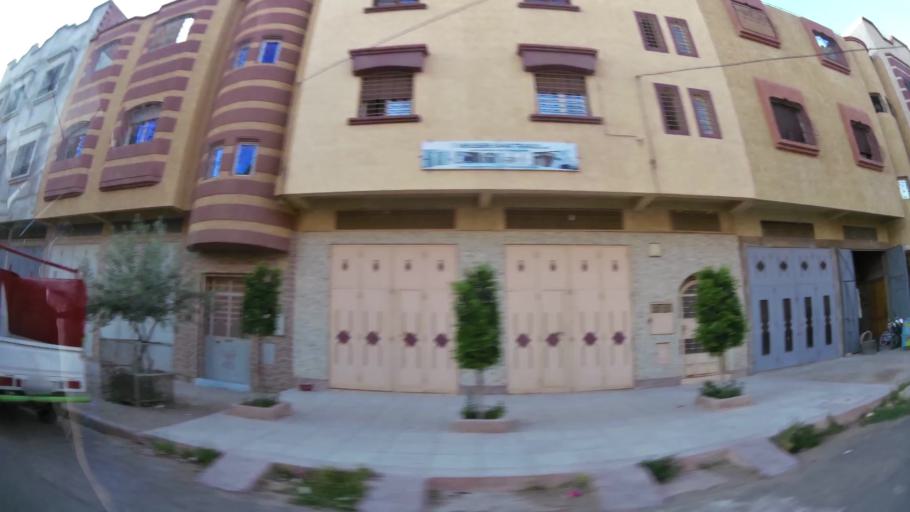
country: MA
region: Oriental
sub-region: Oujda-Angad
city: Oujda
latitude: 34.7144
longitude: -1.9077
